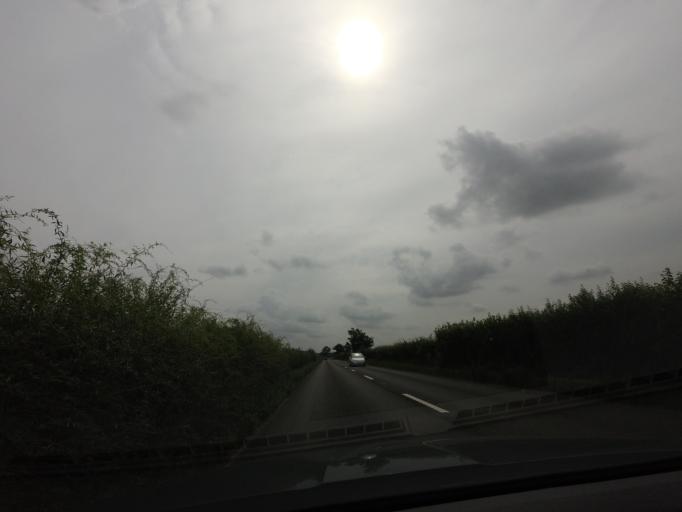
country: GB
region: England
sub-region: Shropshire
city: Tong
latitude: 52.6929
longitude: -2.3176
